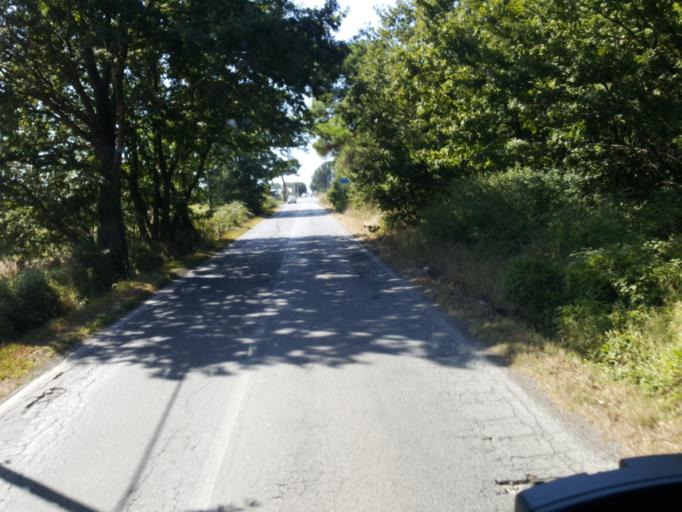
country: IT
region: Latium
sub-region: Citta metropolitana di Roma Capitale
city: Anzio
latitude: 41.5129
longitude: 12.6419
